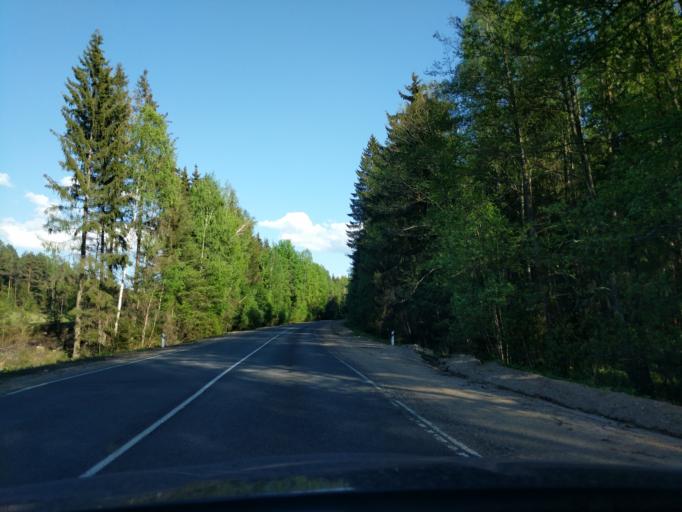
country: BY
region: Minsk
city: Myadzyel
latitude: 54.7660
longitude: 27.0931
